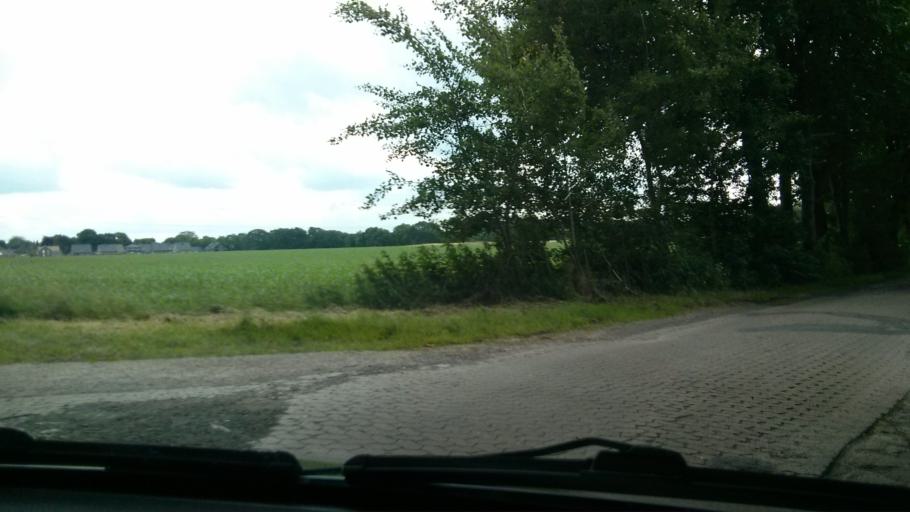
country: DE
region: Lower Saxony
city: Schiffdorf
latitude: 53.5001
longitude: 8.6906
